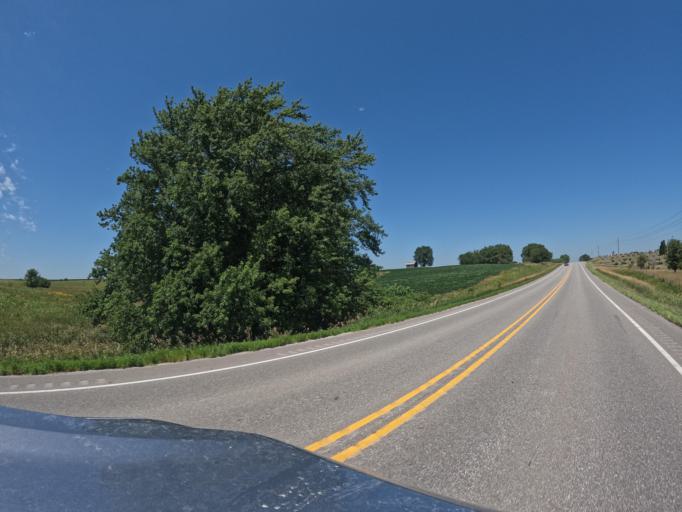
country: US
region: Iowa
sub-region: Keokuk County
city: Sigourney
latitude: 41.4603
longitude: -92.3551
